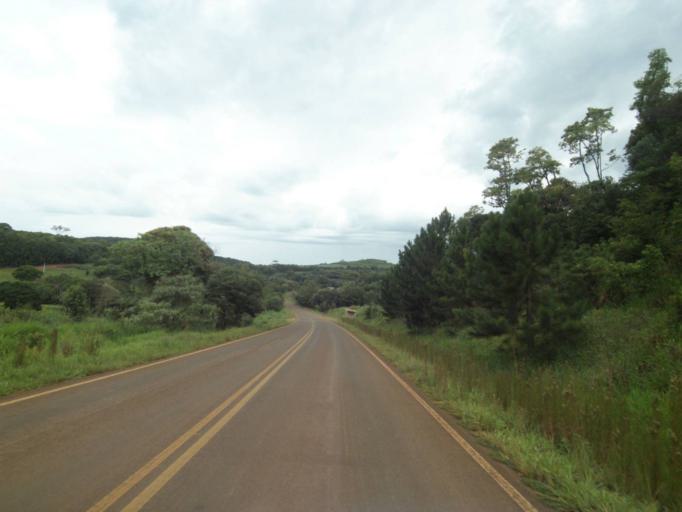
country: BR
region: Parana
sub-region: Pitanga
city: Pitanga
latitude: -24.8968
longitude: -51.9553
